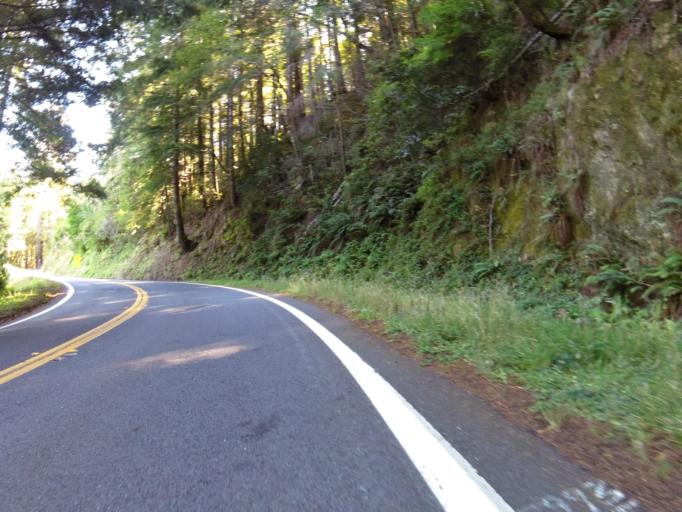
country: US
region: California
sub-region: Mendocino County
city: Fort Bragg
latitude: 39.7253
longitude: -123.8102
